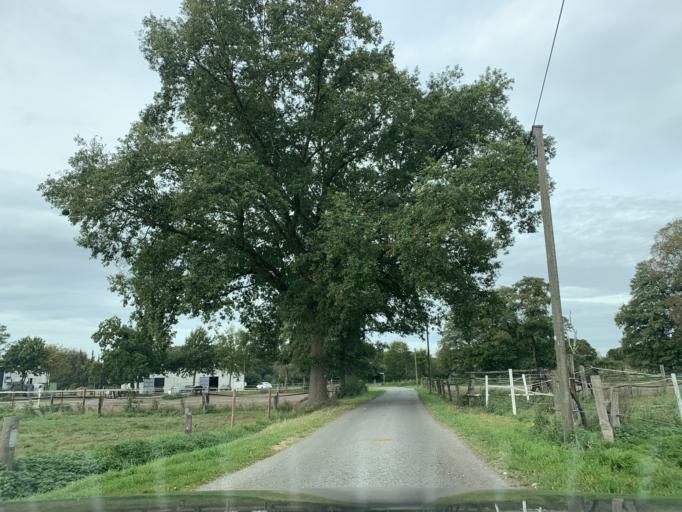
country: DE
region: North Rhine-Westphalia
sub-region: Regierungsbezirk Dusseldorf
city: Hunxe
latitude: 51.6826
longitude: 6.8105
